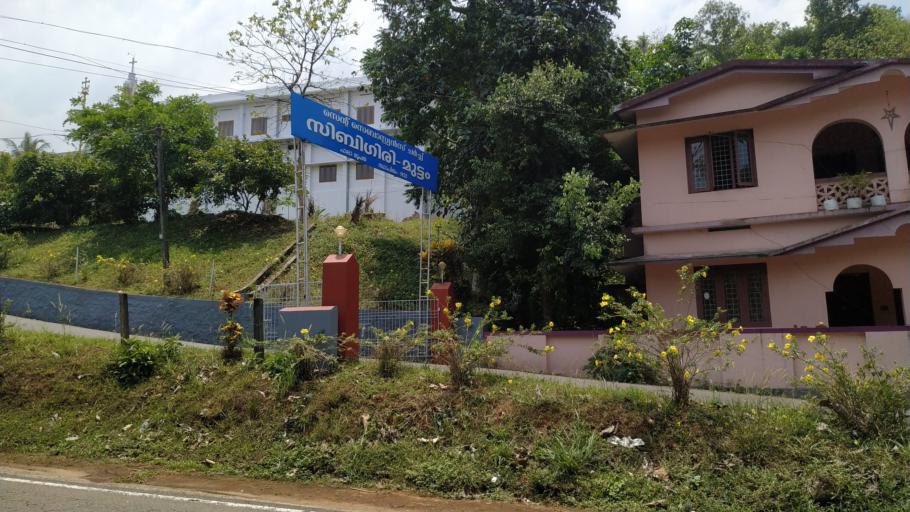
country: IN
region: Kerala
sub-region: Kottayam
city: Lalam
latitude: 9.8360
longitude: 76.7542
